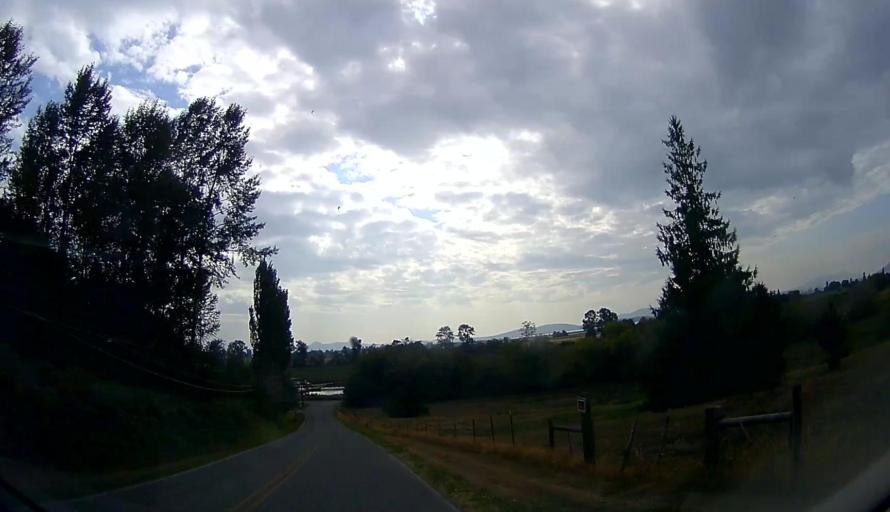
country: US
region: Washington
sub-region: Skagit County
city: Burlington
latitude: 48.5807
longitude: -122.4003
